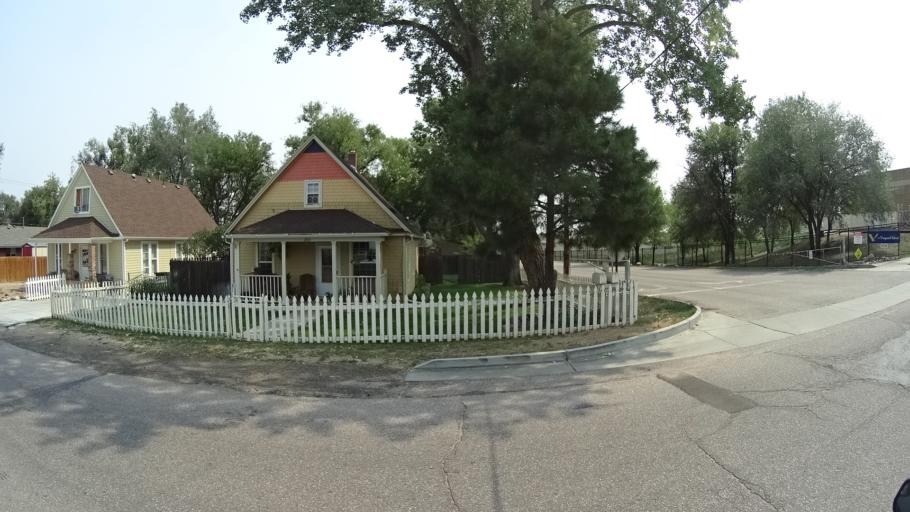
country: US
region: Colorado
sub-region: El Paso County
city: Colorado Springs
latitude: 38.8123
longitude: -104.8176
